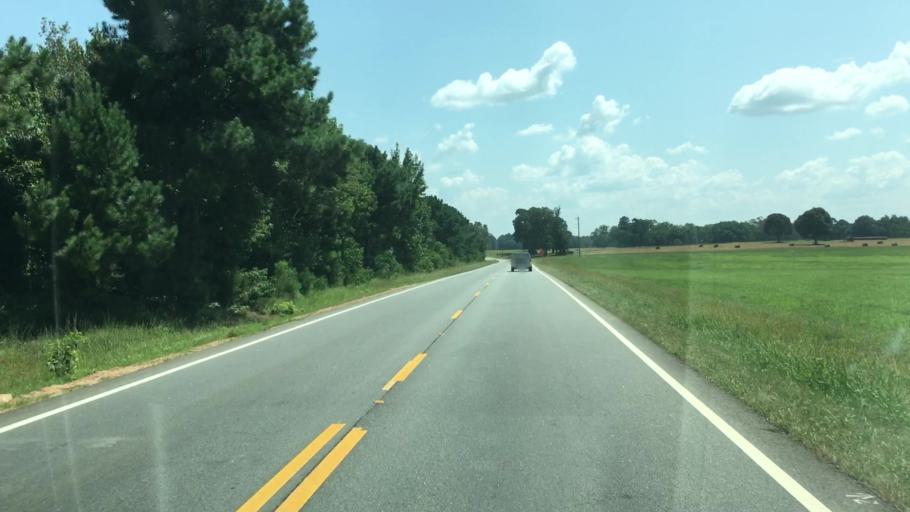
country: US
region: Georgia
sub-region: Oconee County
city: Watkinsville
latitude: 33.8041
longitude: -83.4271
